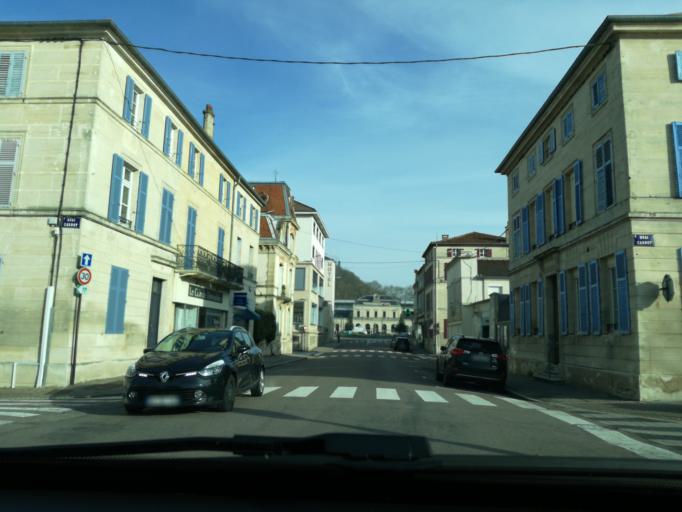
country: FR
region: Lorraine
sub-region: Departement de la Meuse
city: Bar-le-Duc
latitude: 48.7724
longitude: 5.1648
